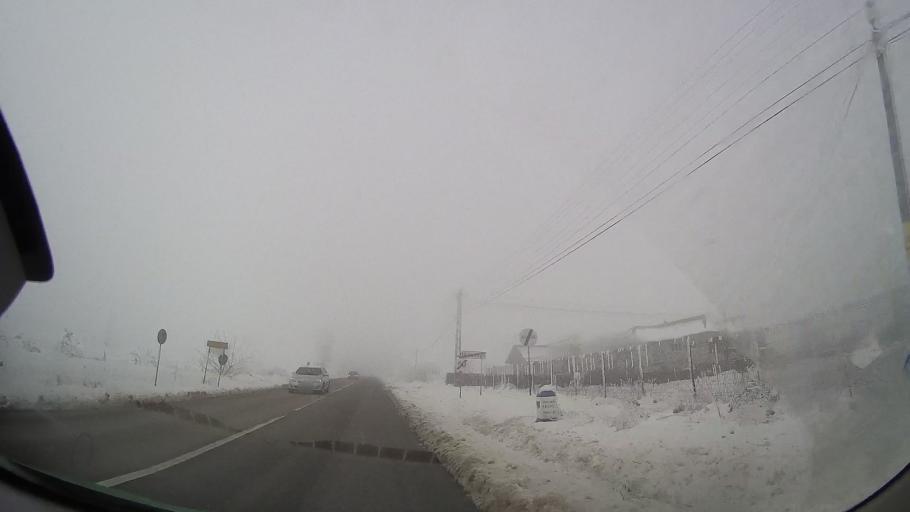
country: RO
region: Iasi
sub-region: Comuna Halaucesti
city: Halaucesti
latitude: 47.1033
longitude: 26.8138
